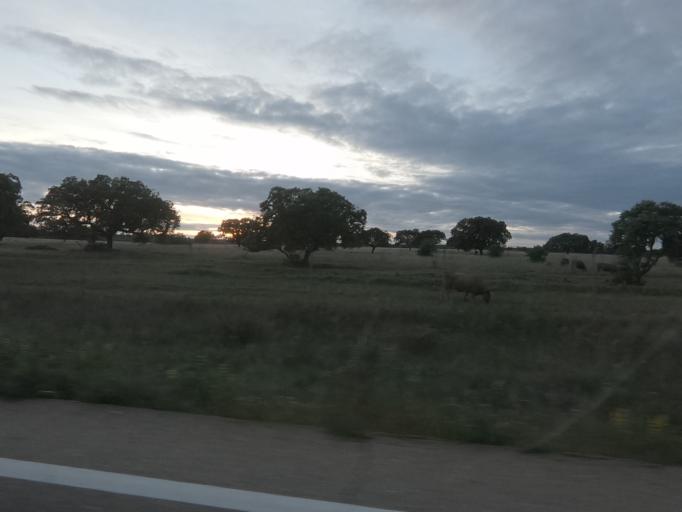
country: ES
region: Extremadura
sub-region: Provincia de Badajoz
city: Villar del Rey
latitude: 39.0223
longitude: -6.8453
